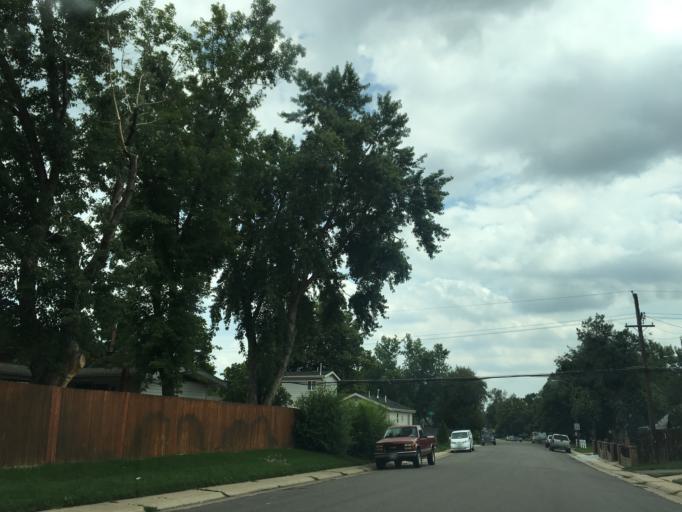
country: US
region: Colorado
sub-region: Arapahoe County
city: Sheridan
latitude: 39.6731
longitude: -105.0349
